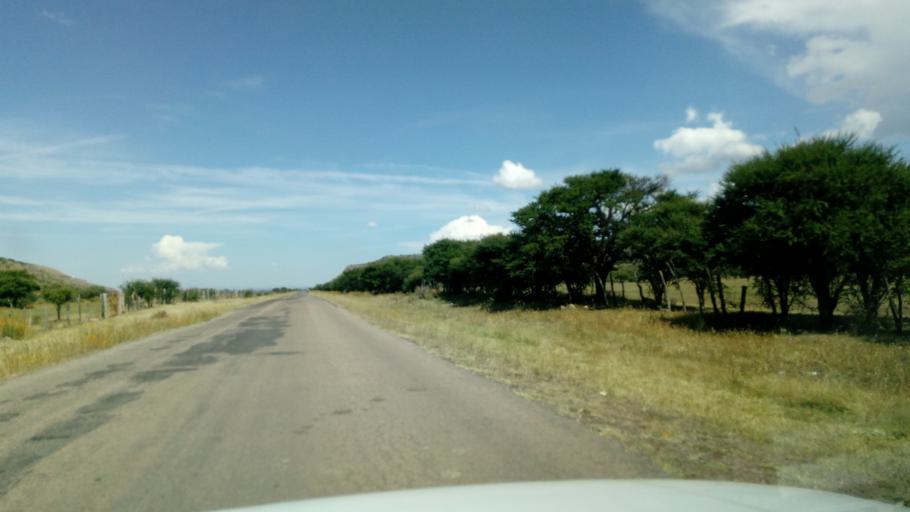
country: MX
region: Durango
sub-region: Durango
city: Jose Refugio Salcido
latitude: 23.8005
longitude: -104.4846
